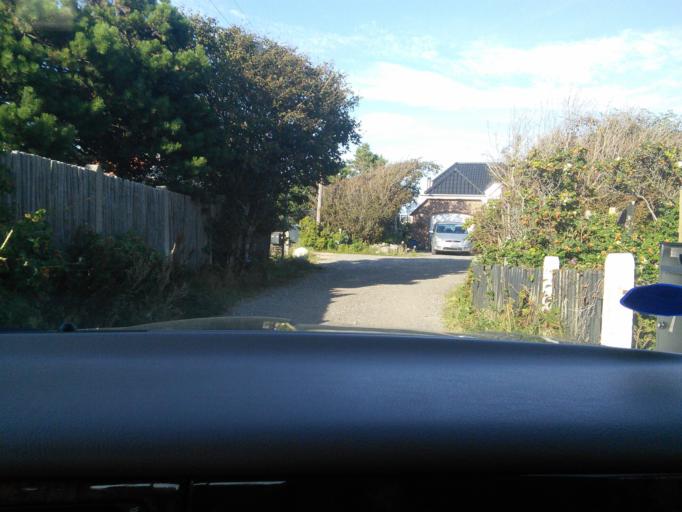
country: DK
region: Capital Region
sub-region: Halsnaes Kommune
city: Liseleje
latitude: 56.0134
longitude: 11.9618
